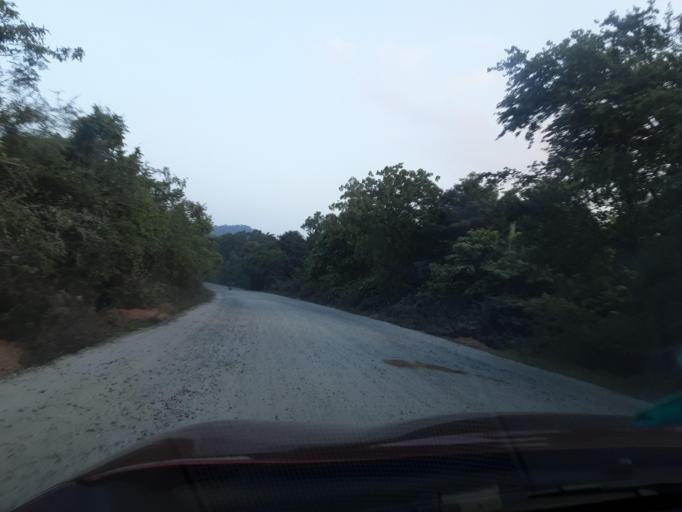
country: LK
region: Central
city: Dambulla
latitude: 7.8060
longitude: 80.7829
